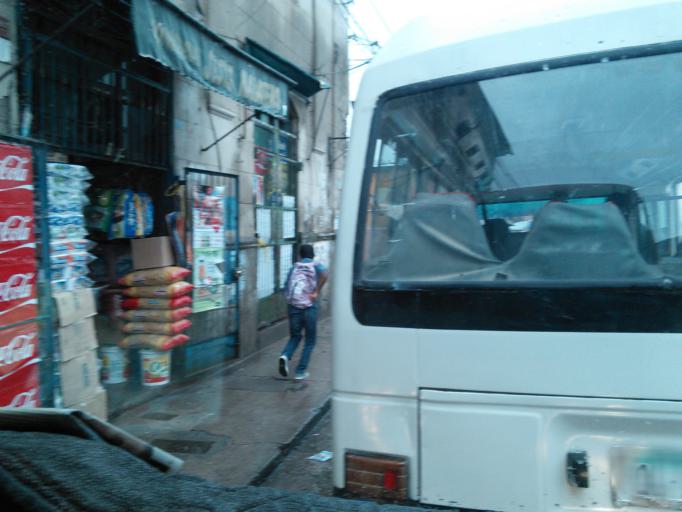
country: PE
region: Ayacucho
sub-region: Provincia de Huamanga
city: Ayacucho
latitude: -13.1653
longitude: -74.2275
